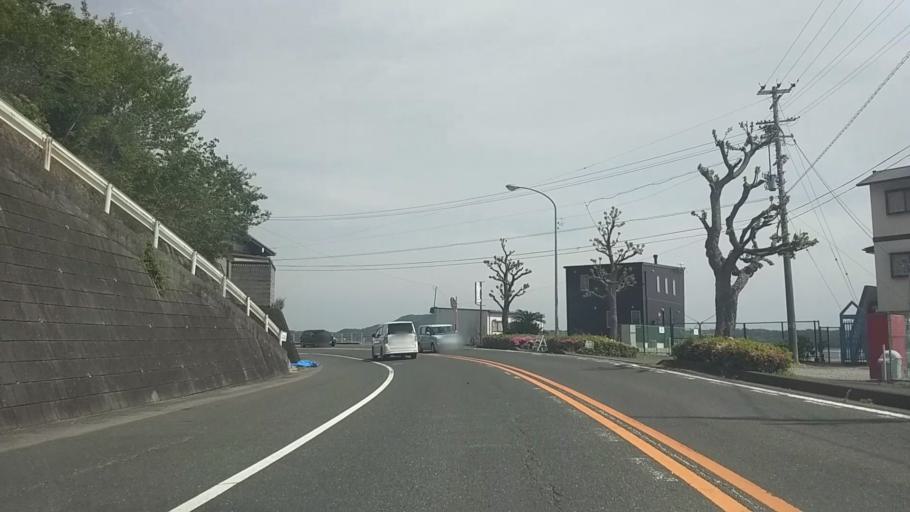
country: JP
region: Shizuoka
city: Kosai-shi
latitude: 34.7931
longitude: 137.6164
